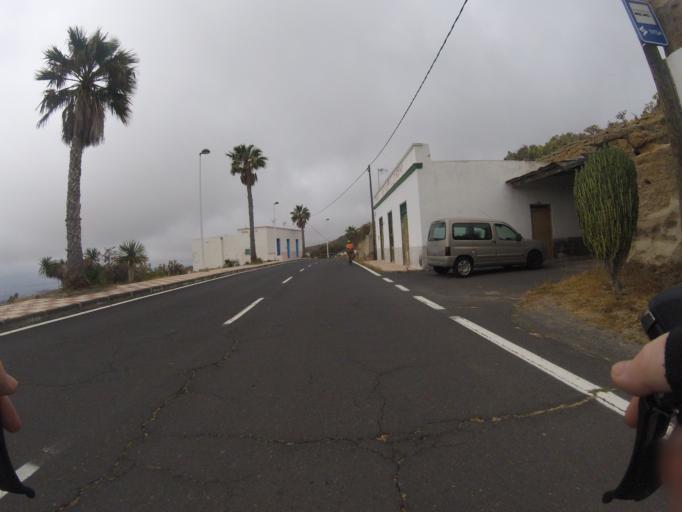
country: ES
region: Canary Islands
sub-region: Provincia de Santa Cruz de Tenerife
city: Fasnia
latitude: 28.2196
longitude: -16.4497
